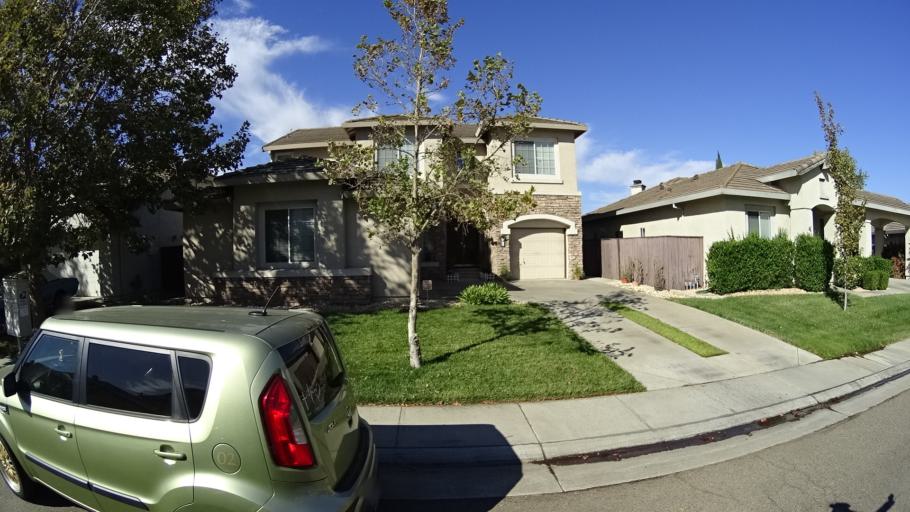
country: US
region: California
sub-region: Sacramento County
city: Laguna
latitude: 38.4221
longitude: -121.4853
